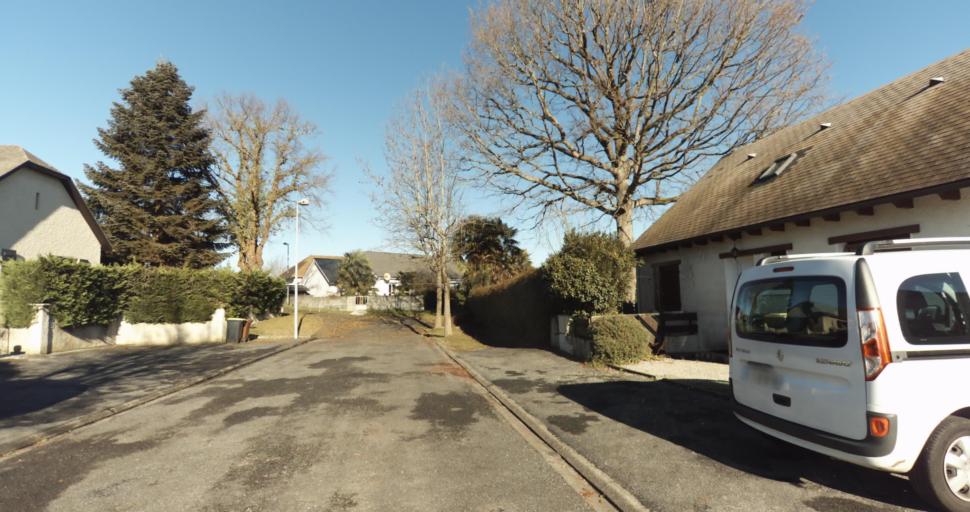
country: FR
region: Aquitaine
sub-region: Departement des Pyrenees-Atlantiques
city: Morlaas
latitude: 43.3483
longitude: -0.2652
